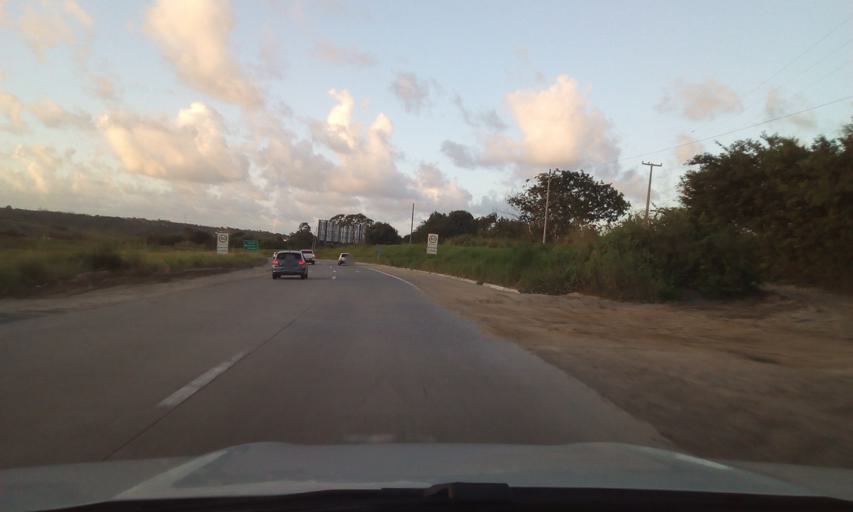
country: BR
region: Pernambuco
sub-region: Itapissuma
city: Itapissuma
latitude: -7.7016
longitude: -34.9225
